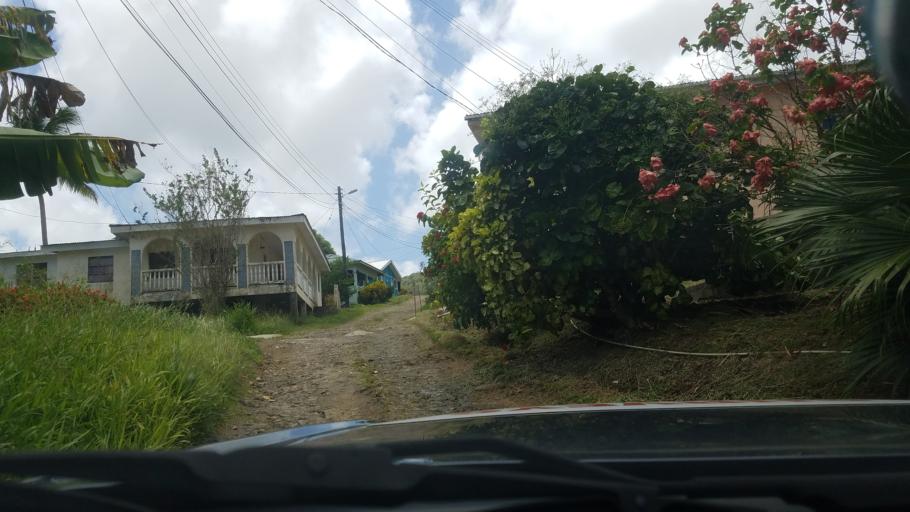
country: LC
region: Gros-Islet
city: Gros Islet
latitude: 14.0547
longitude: -60.9323
